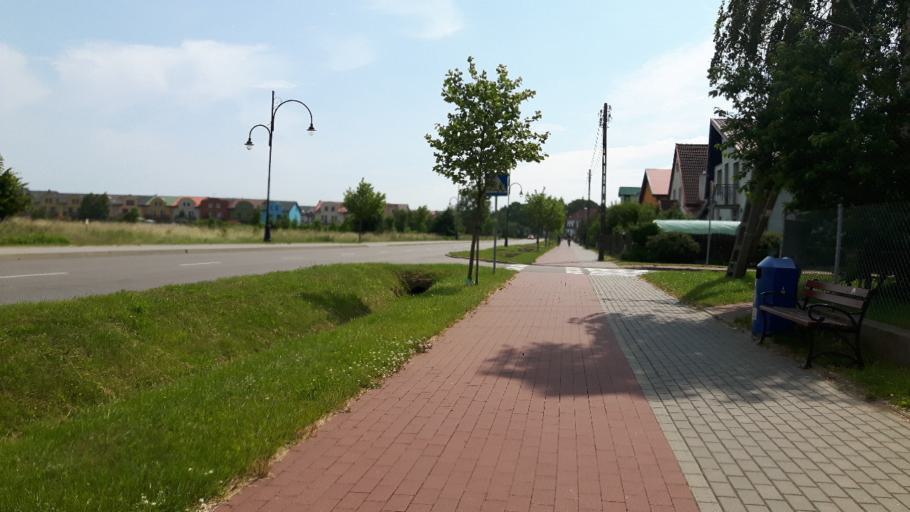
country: PL
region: Pomeranian Voivodeship
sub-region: Powiat leborski
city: Leba
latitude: 54.7500
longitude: 17.5681
